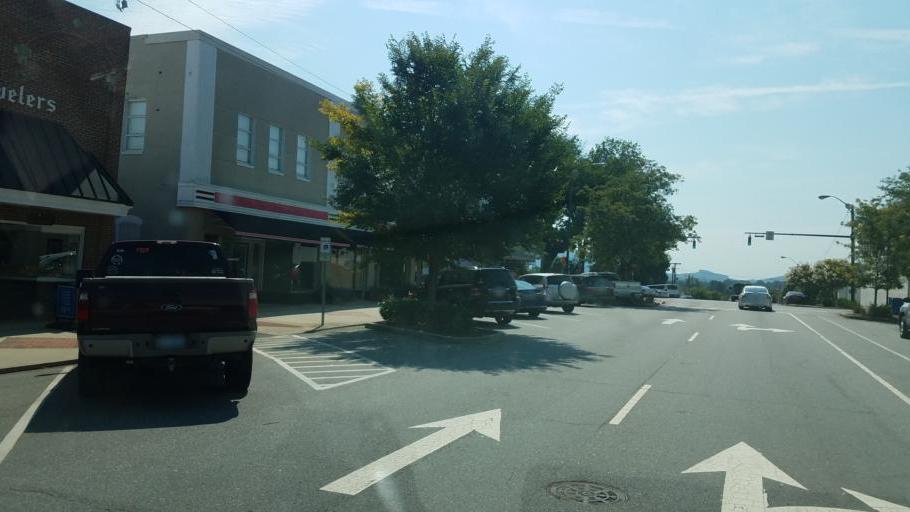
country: US
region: North Carolina
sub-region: Burke County
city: Morganton
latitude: 35.7459
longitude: -81.6887
